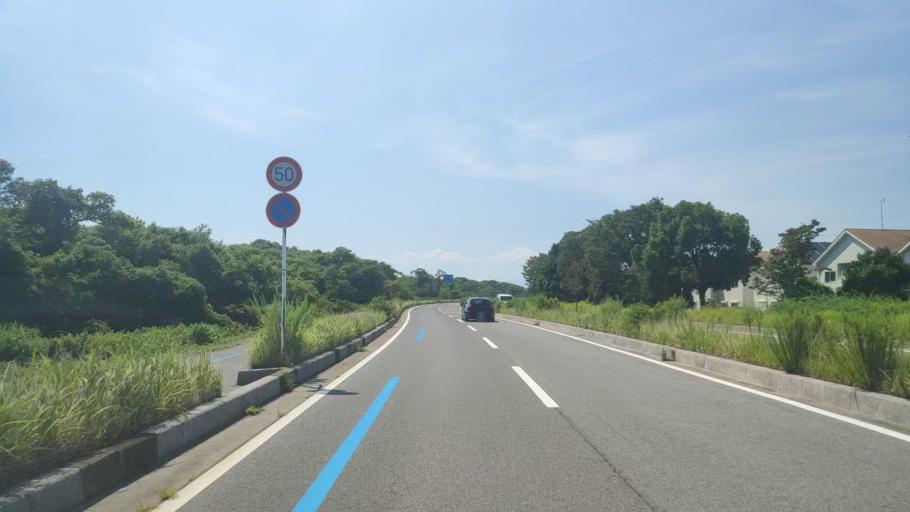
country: JP
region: Shiga Prefecture
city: Nagahama
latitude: 35.3837
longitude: 136.2515
